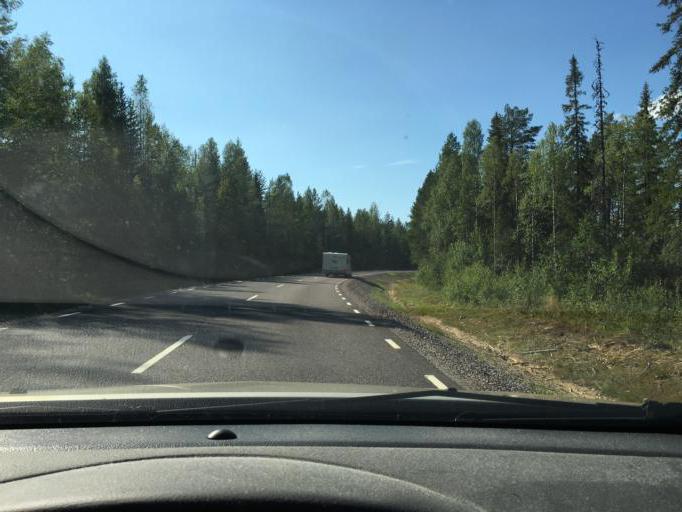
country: SE
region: Norrbotten
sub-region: Lulea Kommun
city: Ranea
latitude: 66.0482
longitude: 22.2392
